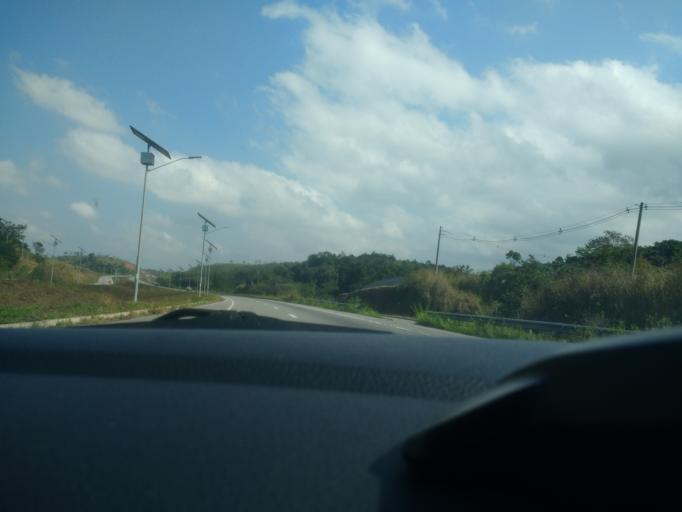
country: BR
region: Rio de Janeiro
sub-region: Queimados
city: Queimados
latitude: -22.6866
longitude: -43.5043
